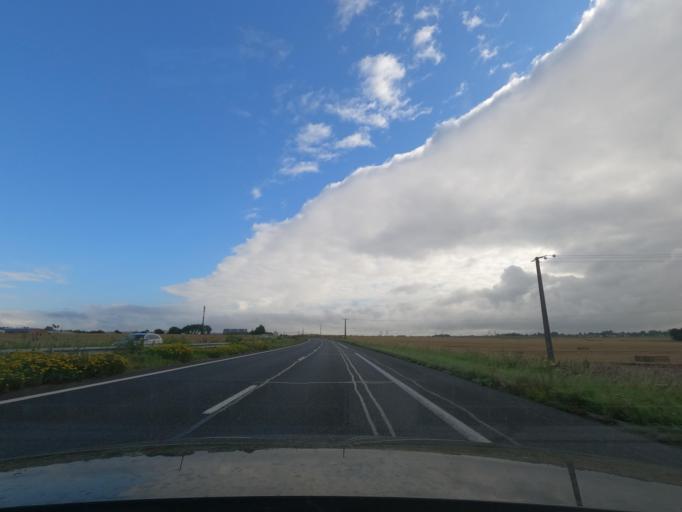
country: FR
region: Haute-Normandie
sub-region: Departement de la Seine-Maritime
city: Blainville-Crevon
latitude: 49.5638
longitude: 1.2718
